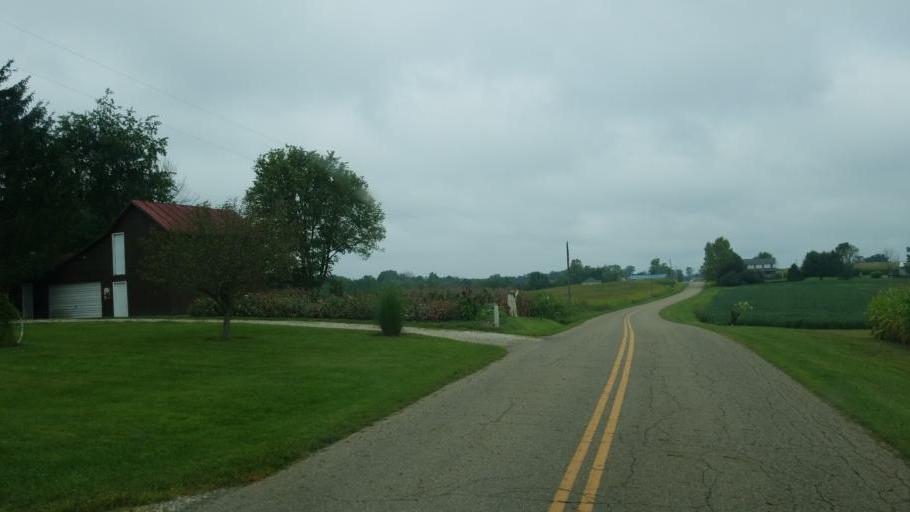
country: US
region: Ohio
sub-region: Licking County
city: Utica
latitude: 40.2733
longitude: -82.4155
